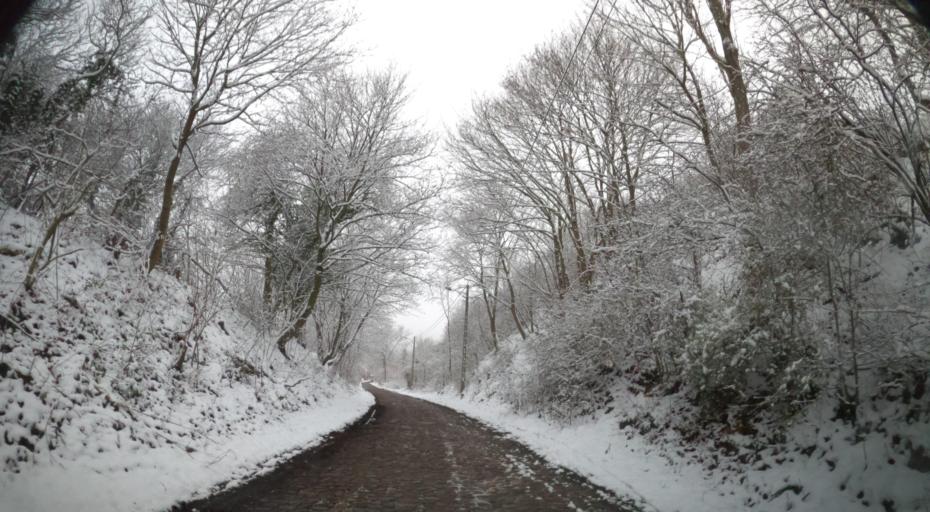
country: PL
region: West Pomeranian Voivodeship
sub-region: Szczecin
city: Szczecin
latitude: 53.3441
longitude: 14.5645
